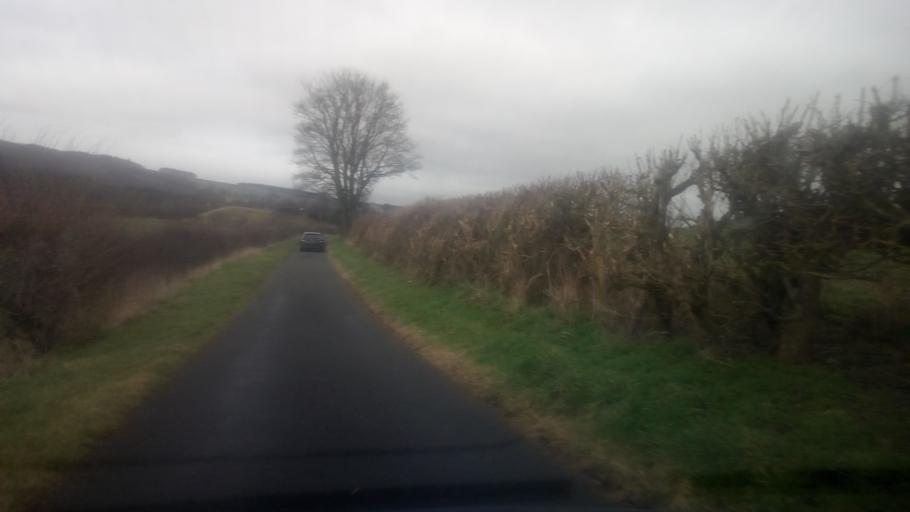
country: GB
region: Scotland
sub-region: The Scottish Borders
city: Jedburgh
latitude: 55.5006
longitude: -2.5389
